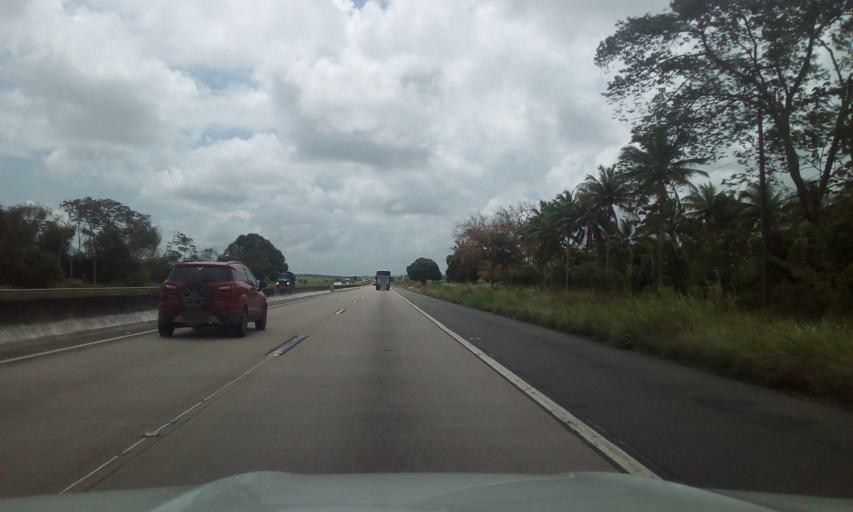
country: BR
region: Pernambuco
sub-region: Goiana
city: Goiana
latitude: -7.6419
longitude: -34.9549
